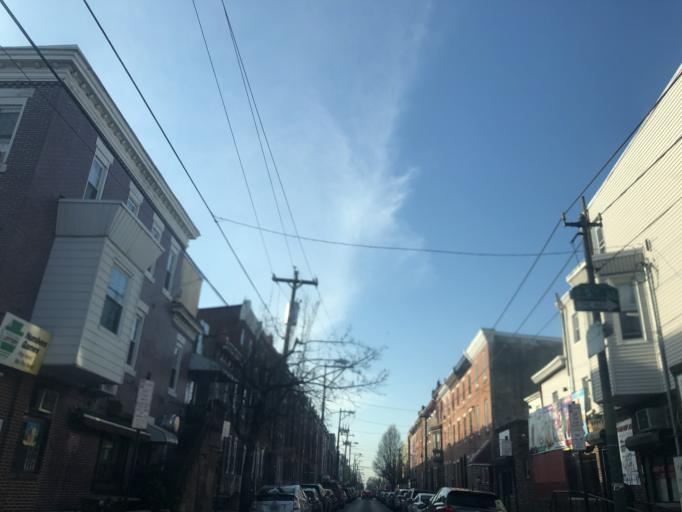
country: US
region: Pennsylvania
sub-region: Philadelphia County
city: Philadelphia
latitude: 39.9286
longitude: -75.1537
